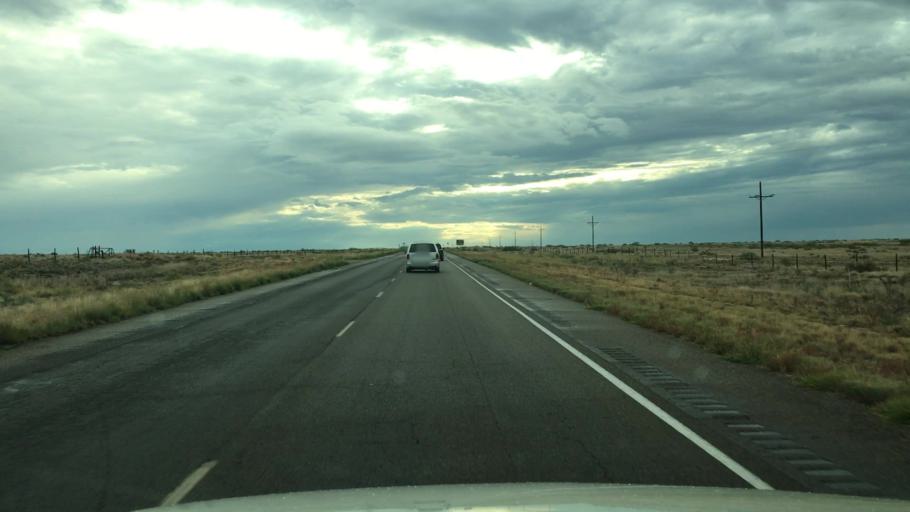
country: US
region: New Mexico
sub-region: Chaves County
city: Roswell
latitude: 33.4026
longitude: -104.3268
